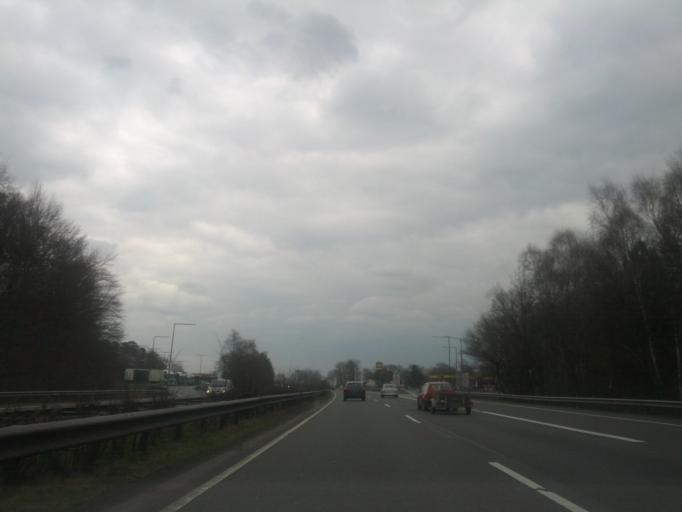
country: DE
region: Lower Saxony
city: Ganderkesee
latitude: 53.0557
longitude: 8.4967
